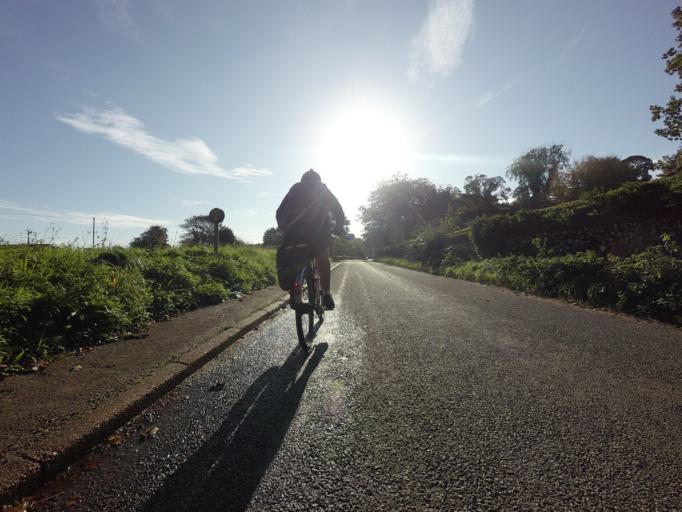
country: GB
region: England
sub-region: Norfolk
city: Dersingham
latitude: 52.8349
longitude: 0.5836
